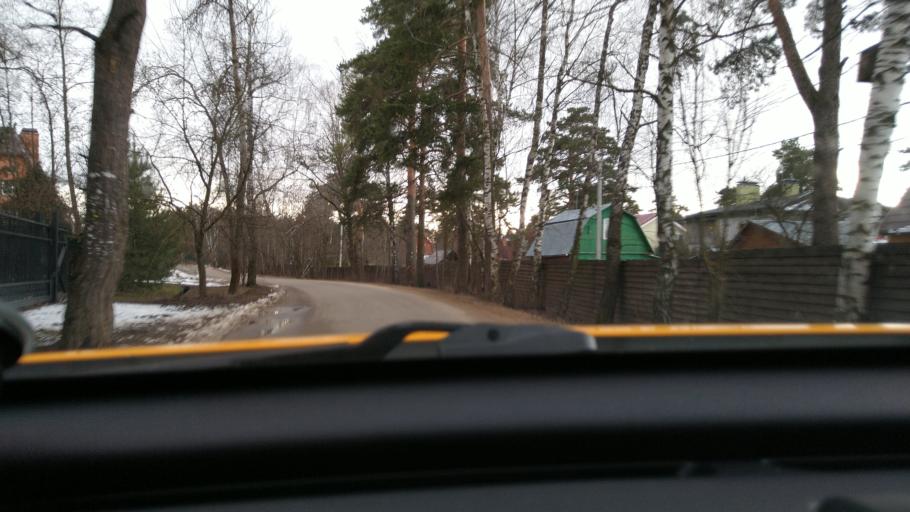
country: RU
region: Moskovskaya
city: Petrovo-Dal'neye
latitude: 55.7651
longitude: 37.2058
